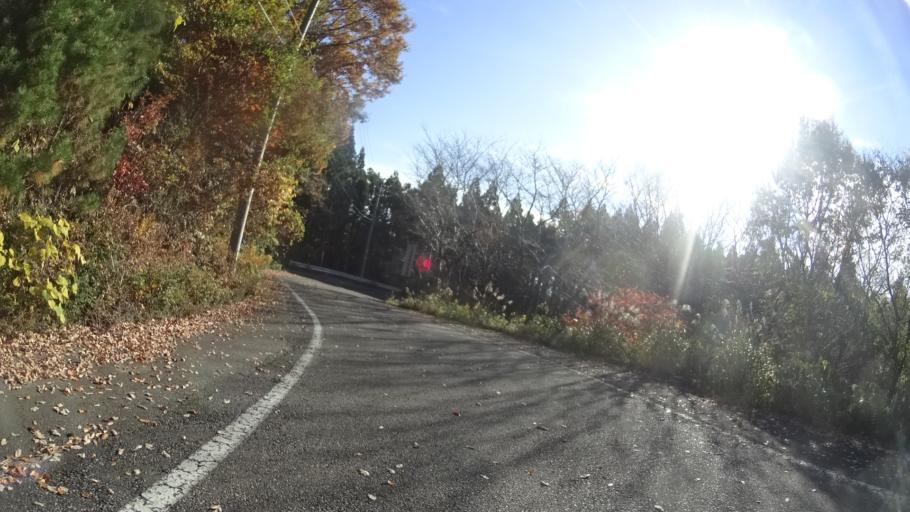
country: JP
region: Niigata
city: Yoshida-kasugacho
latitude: 37.6632
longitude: 138.8148
